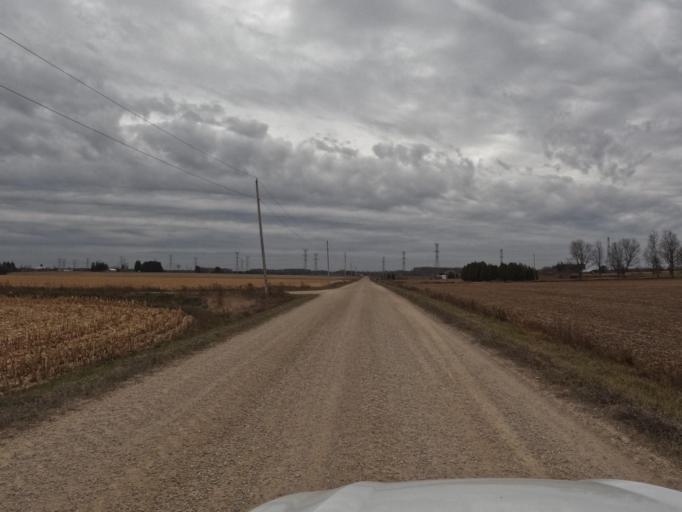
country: CA
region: Ontario
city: Shelburne
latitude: 43.9962
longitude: -80.3860
